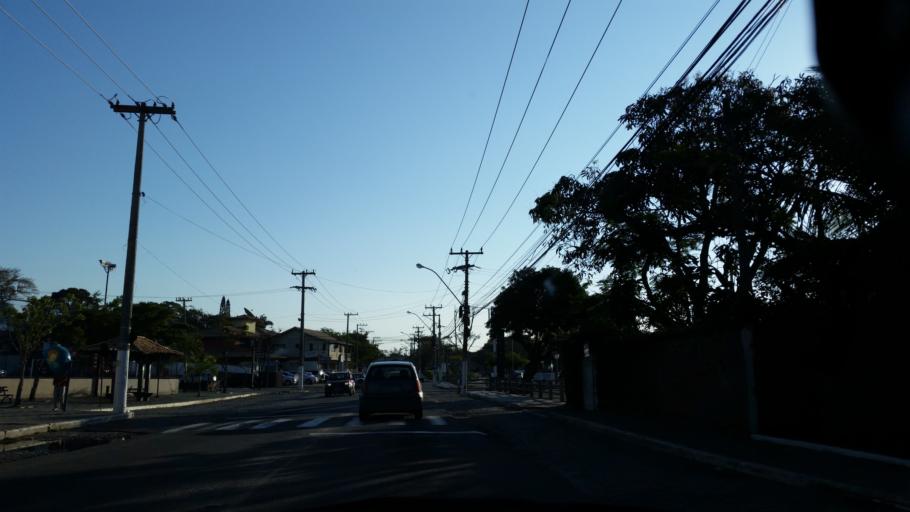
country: BR
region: Rio de Janeiro
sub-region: Armacao De Buzios
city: Armacao de Buzios
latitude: -22.7693
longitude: -41.9097
